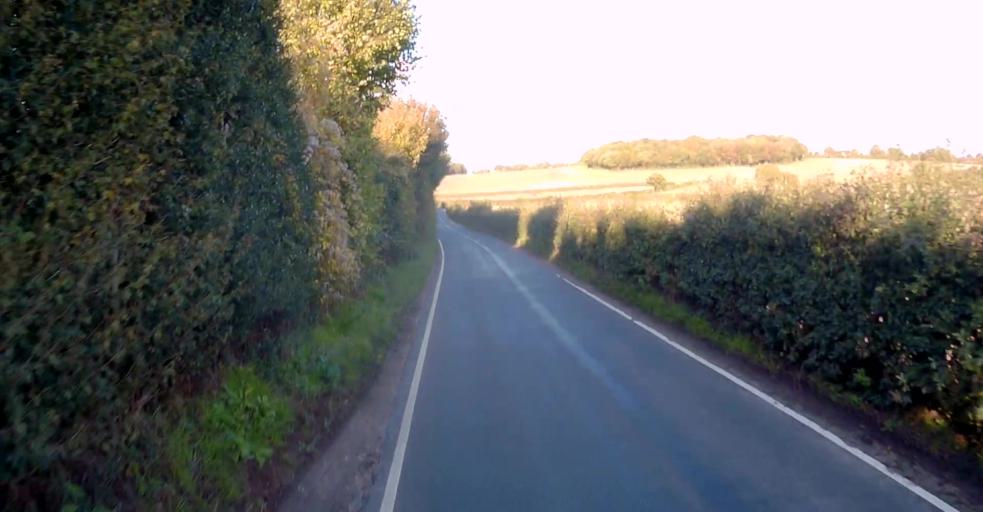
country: GB
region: England
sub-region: Hampshire
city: Long Sutton
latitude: 51.2340
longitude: -0.9264
